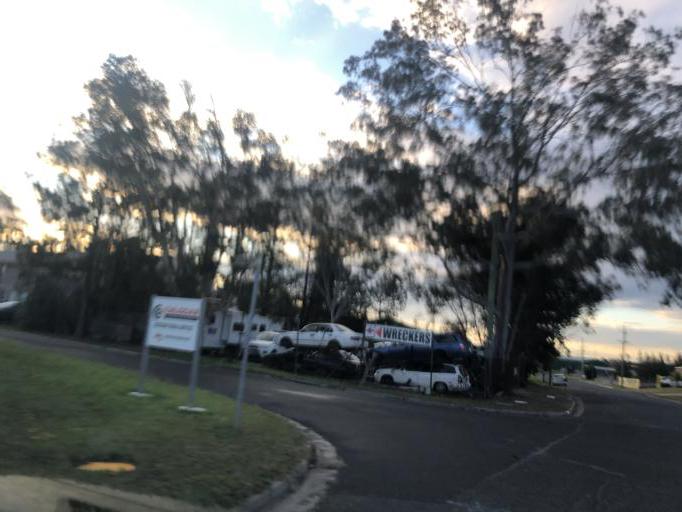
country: AU
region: New South Wales
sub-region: Nambucca Shire
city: Macksville
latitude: -30.7277
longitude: 152.9127
